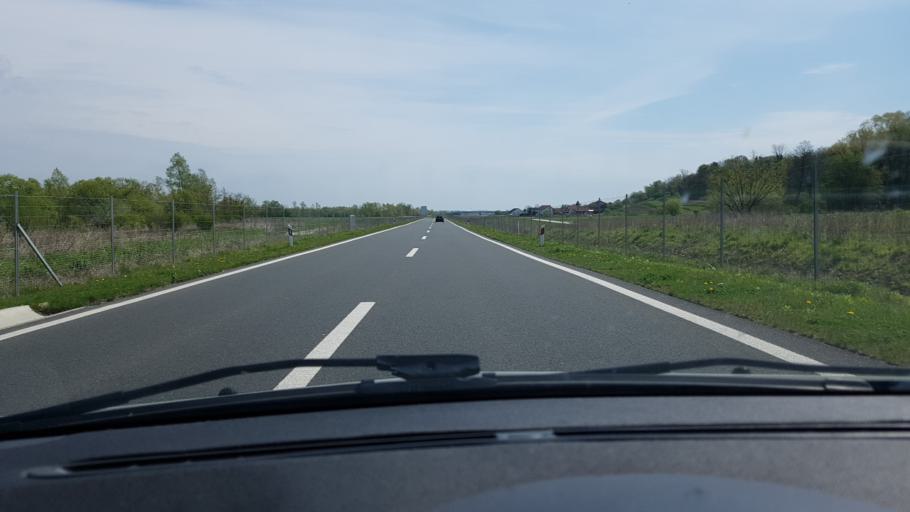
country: HR
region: Krapinsko-Zagorska
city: Selnica
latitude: 46.0374
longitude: 16.0346
